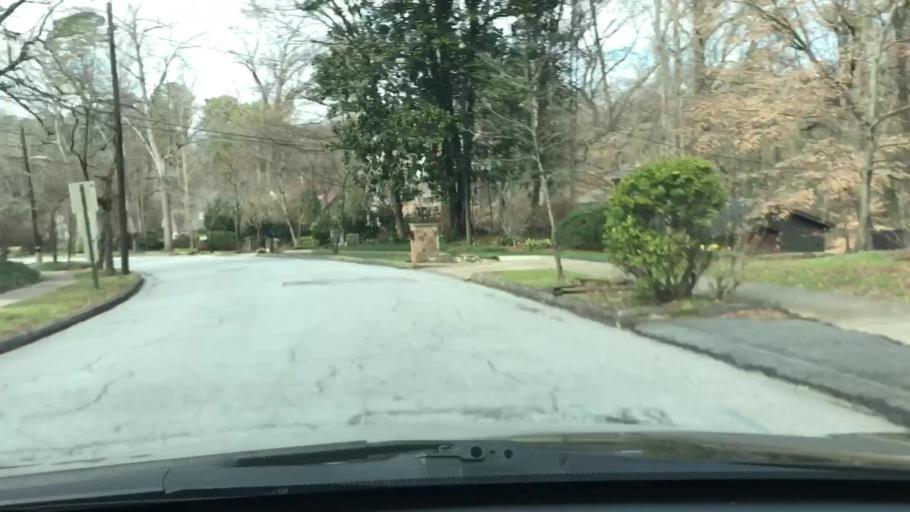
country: US
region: Georgia
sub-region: DeKalb County
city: Druid Hills
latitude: 33.7830
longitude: -84.3206
